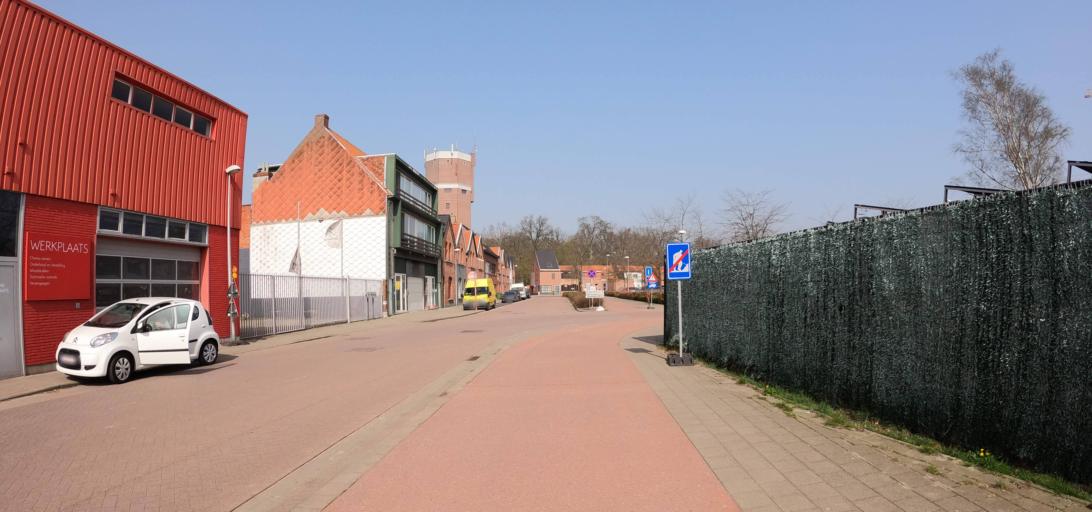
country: BE
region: Flanders
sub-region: Provincie Antwerpen
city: Kapellen
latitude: 51.3140
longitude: 4.4254
